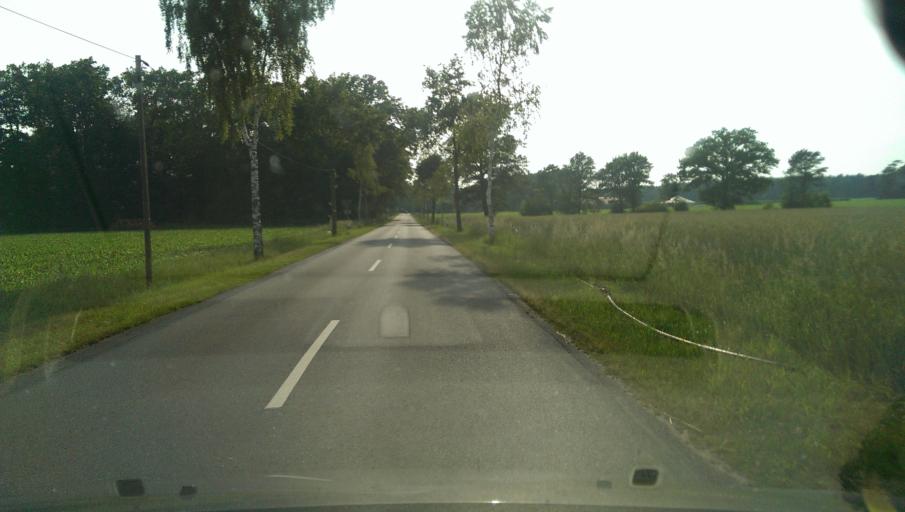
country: DE
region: Lower Saxony
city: Munster
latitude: 52.9185
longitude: 10.0637
